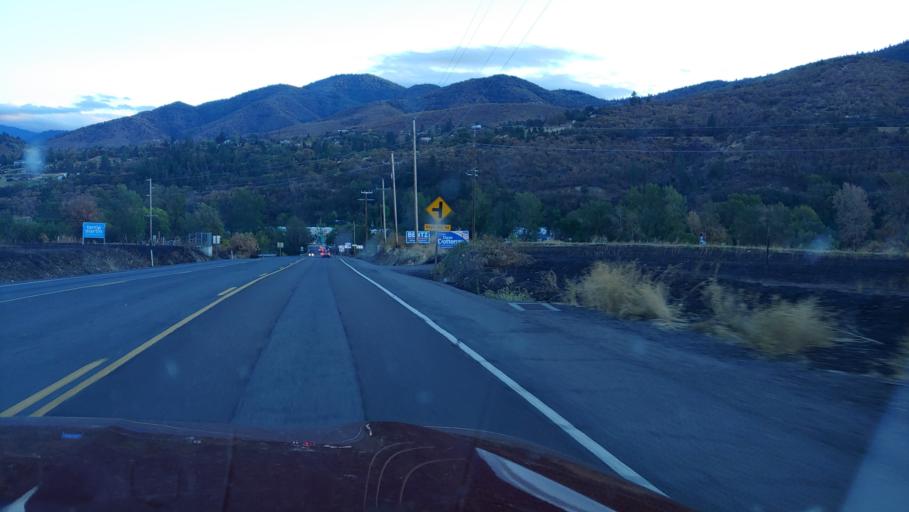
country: US
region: Oregon
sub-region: Jackson County
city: Ashland
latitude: 42.2248
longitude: -122.7406
